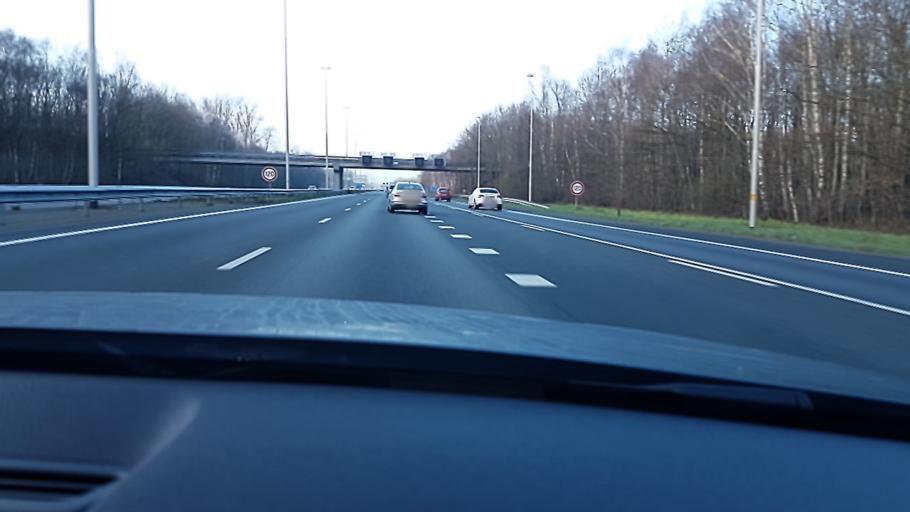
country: NL
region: Overijssel
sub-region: Gemeente Borne
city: Borne
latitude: 52.2919
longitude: 6.7312
